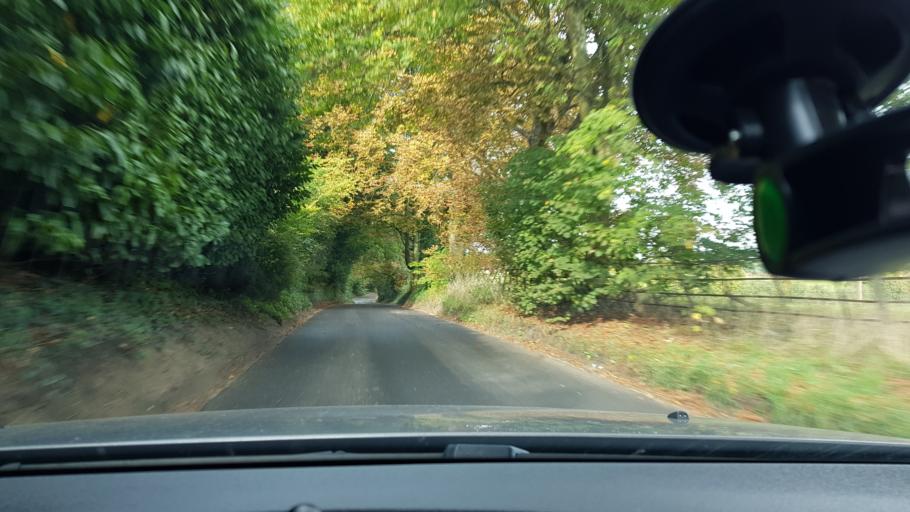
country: GB
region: England
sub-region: West Berkshire
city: Kintbury
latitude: 51.4070
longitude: -1.4804
